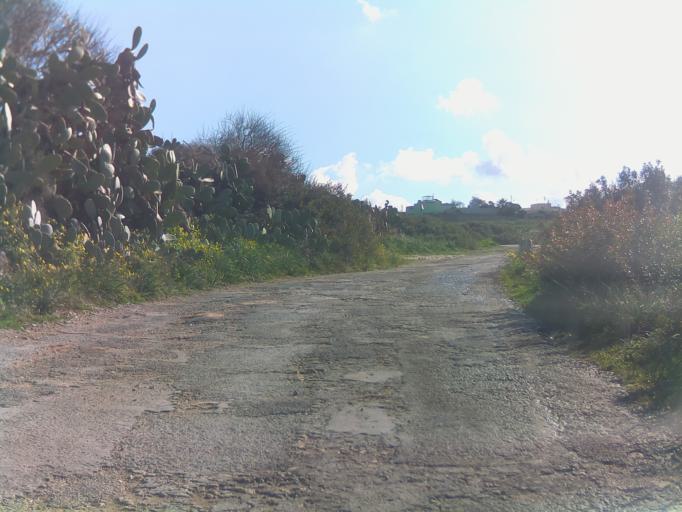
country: MT
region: L-Imgarr
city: Imgarr
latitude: 35.8993
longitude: 14.3610
